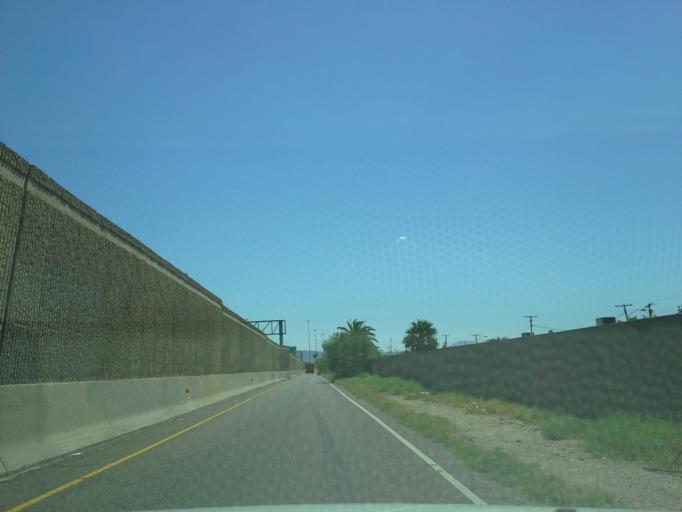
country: US
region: Arizona
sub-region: Maricopa County
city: Phoenix
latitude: 33.4871
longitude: -112.1134
